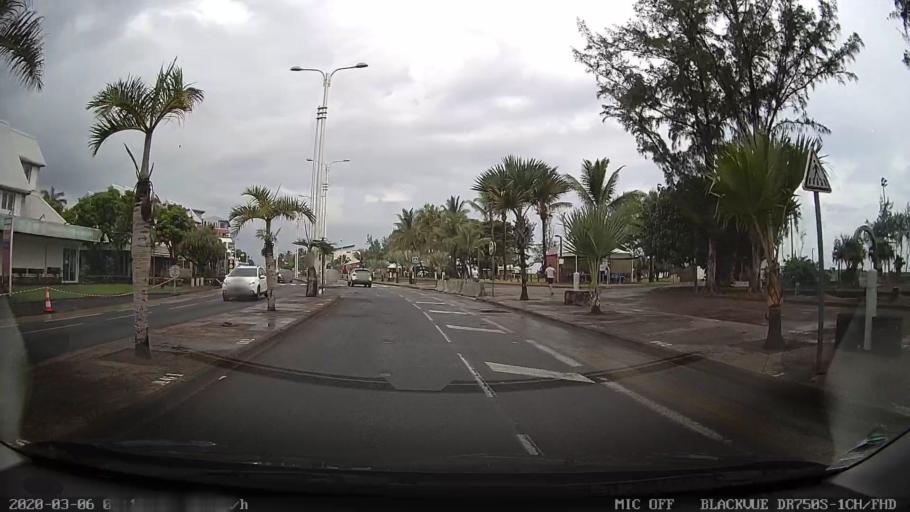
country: RE
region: Reunion
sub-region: Reunion
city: Saint-Pierre
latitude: -21.3413
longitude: 55.4590
